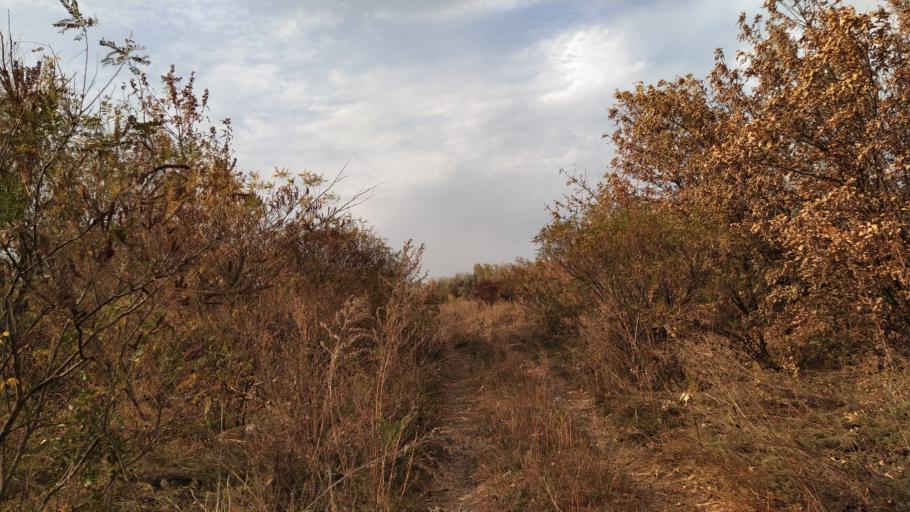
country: RU
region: Rostov
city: Kuleshovka
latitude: 47.1424
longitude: 39.5856
